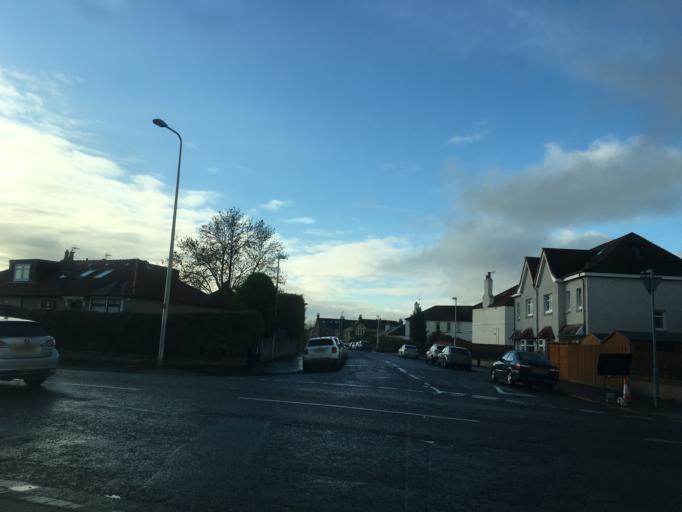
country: GB
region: Scotland
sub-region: Edinburgh
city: Colinton
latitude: 55.9412
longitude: -3.2515
